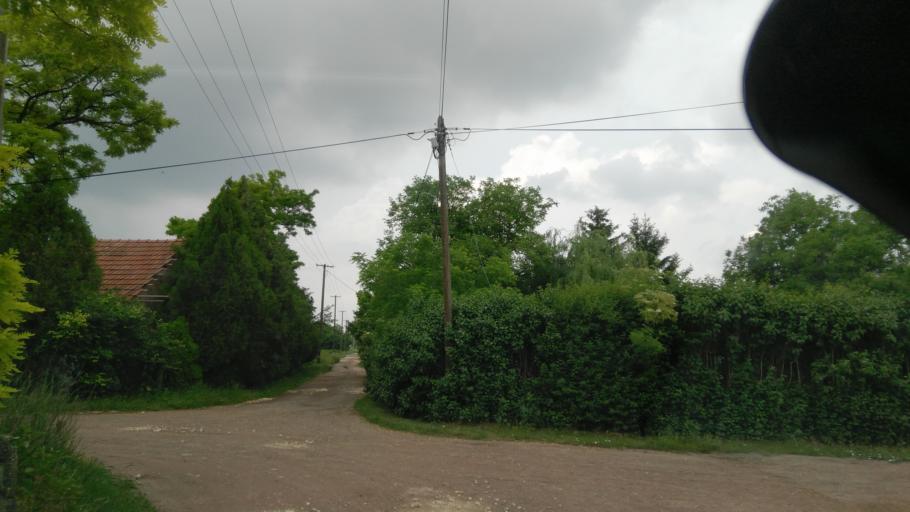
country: HU
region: Bekes
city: Bekescsaba
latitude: 46.7091
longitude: 21.1415
